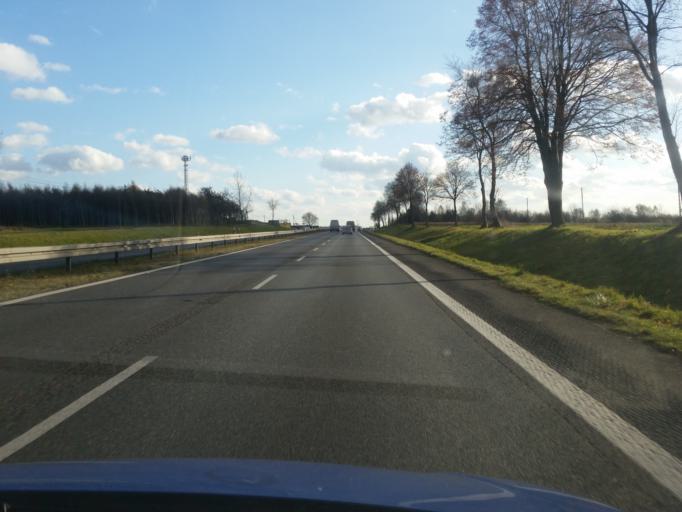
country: PL
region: Silesian Voivodeship
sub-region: Powiat myszkowski
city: Kozieglowy
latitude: 50.6119
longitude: 19.1529
